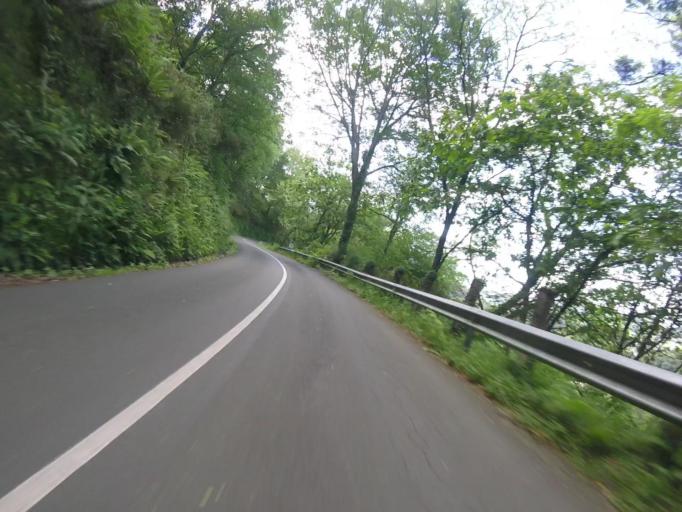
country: ES
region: Basque Country
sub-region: Provincia de Guipuzcoa
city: Errenteria
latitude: 43.2747
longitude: -1.8488
